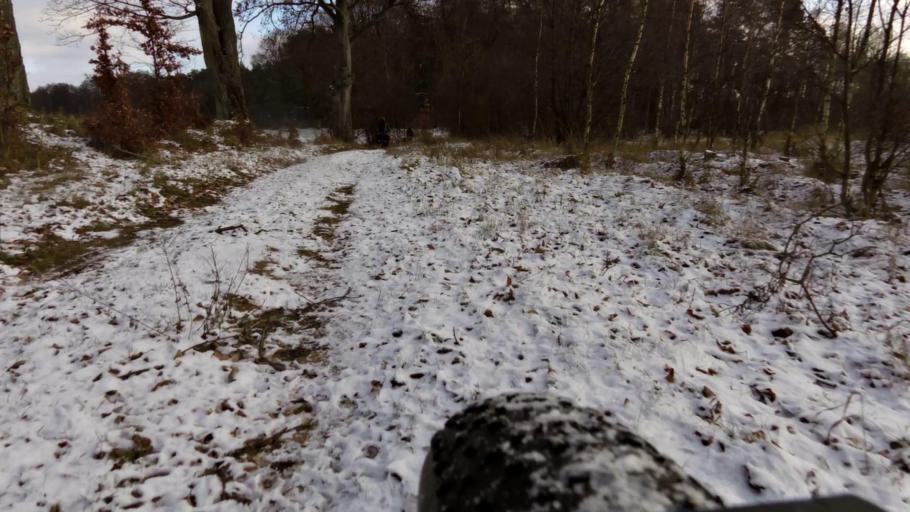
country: PL
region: West Pomeranian Voivodeship
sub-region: Powiat walecki
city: Tuczno
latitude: 53.2997
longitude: 16.2852
